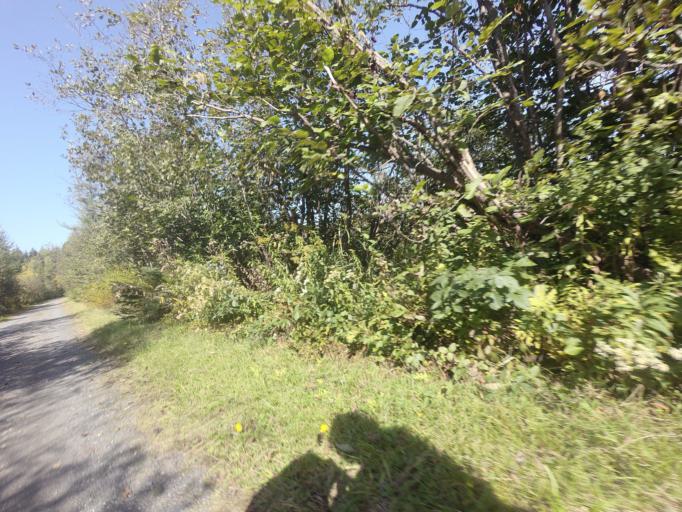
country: CA
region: Quebec
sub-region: Laurentides
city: Sainte-Agathe-des-Monts
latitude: 46.0673
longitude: -74.3124
